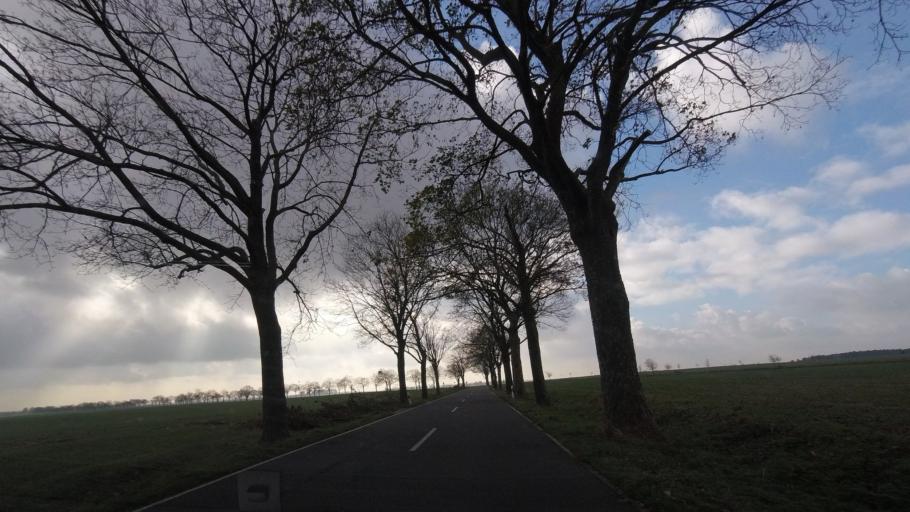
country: DE
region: Brandenburg
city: Niedergorsdorf
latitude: 52.0011
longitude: 12.9348
